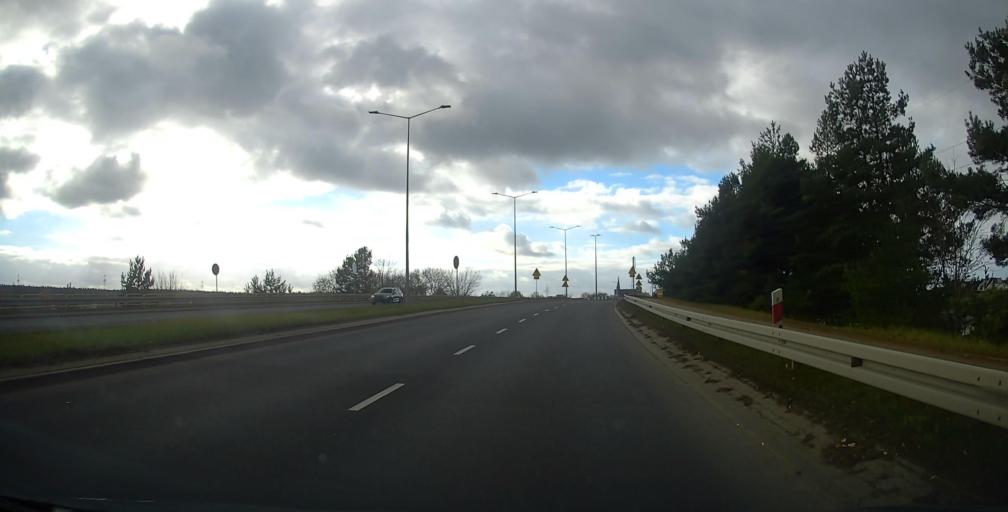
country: PL
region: Warmian-Masurian Voivodeship
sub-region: Powiat elcki
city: Elk
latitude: 53.8085
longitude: 22.3740
